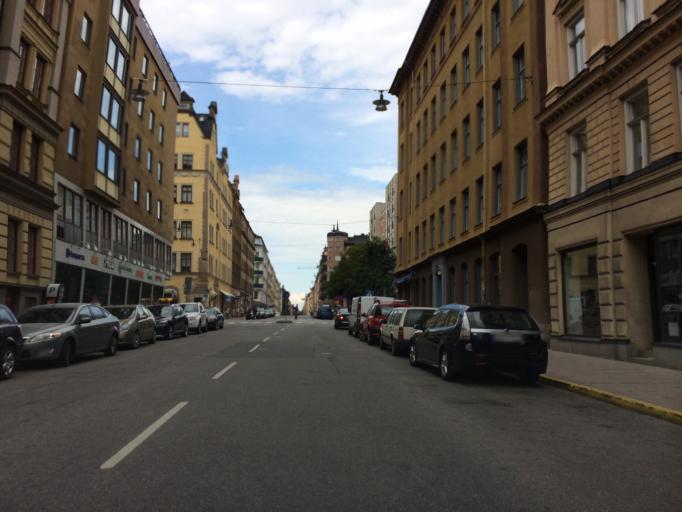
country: SE
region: Stockholm
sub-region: Stockholms Kommun
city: Stockholm
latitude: 59.3392
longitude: 18.0520
